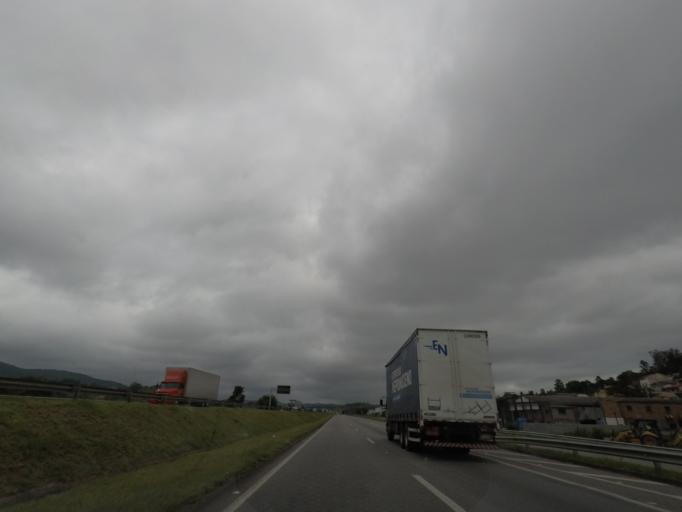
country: BR
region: Sao Paulo
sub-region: Bom Jesus Dos Perdoes
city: Bom Jesus dos Perdoes
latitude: -23.1367
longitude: -46.4597
